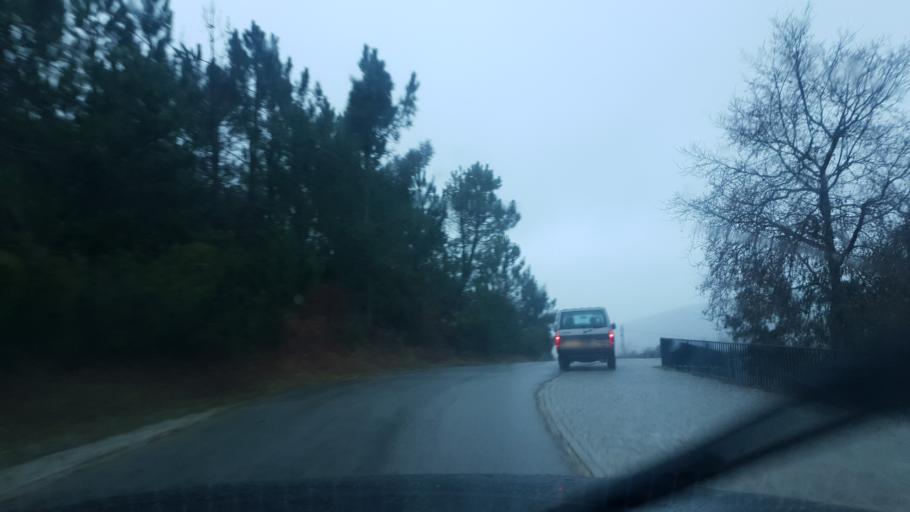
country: PT
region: Viseu
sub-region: Oliveira de Frades
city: Oliveira de Frades
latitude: 40.8271
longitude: -8.1502
